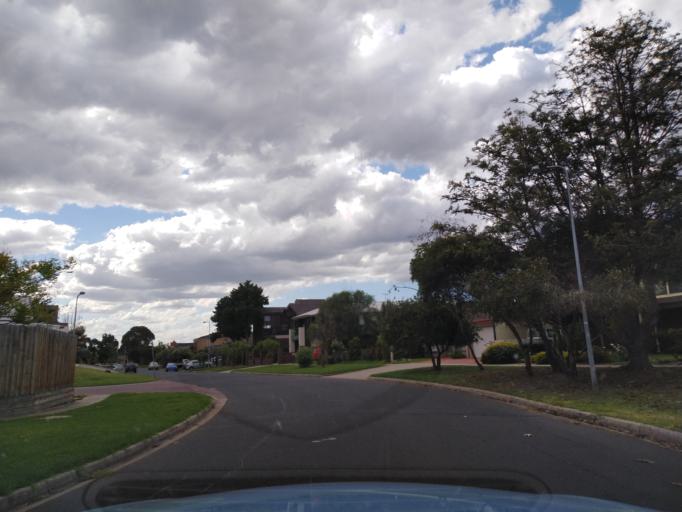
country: AU
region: Victoria
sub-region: Hobsons Bay
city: Williamstown North
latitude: -37.8555
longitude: 144.8741
